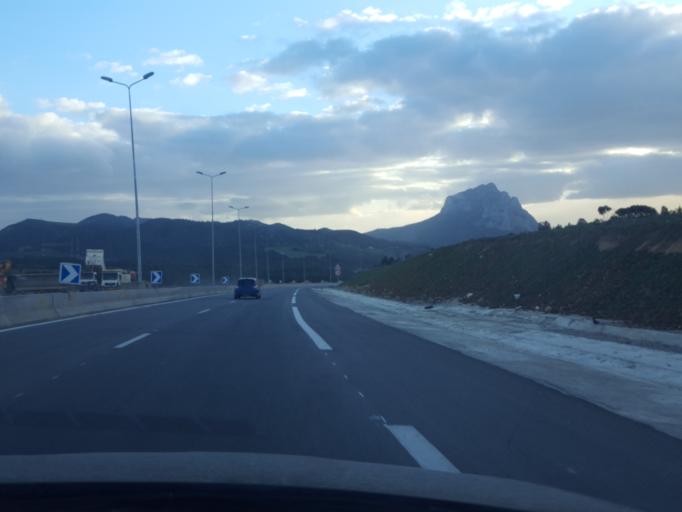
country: TN
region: Tunis
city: Hammam-Lif
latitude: 36.6554
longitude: 10.3724
